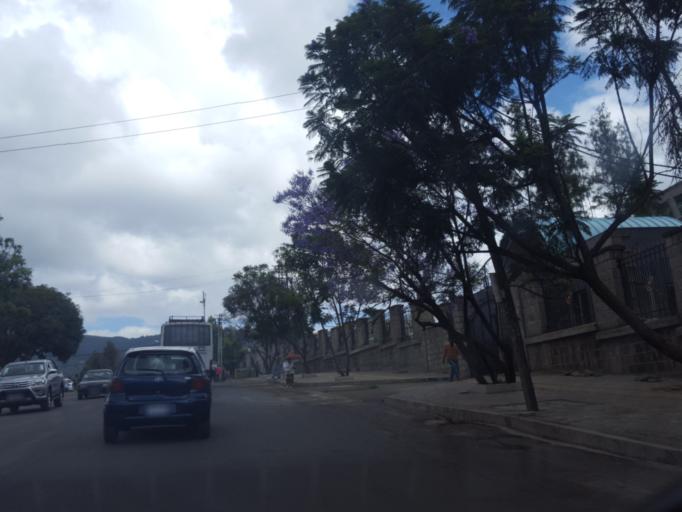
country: ET
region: Adis Abeba
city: Addis Ababa
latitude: 9.0561
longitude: 38.7628
